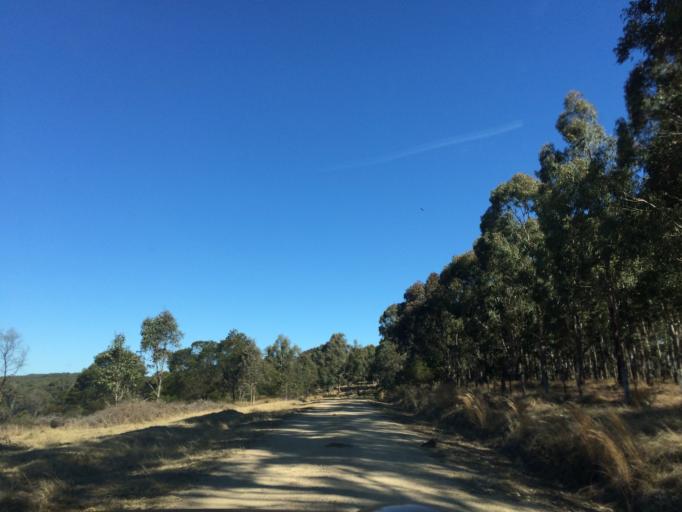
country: AU
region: New South Wales
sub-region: Tenterfield Municipality
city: Carrolls Creek
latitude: -28.6391
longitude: 152.1737
